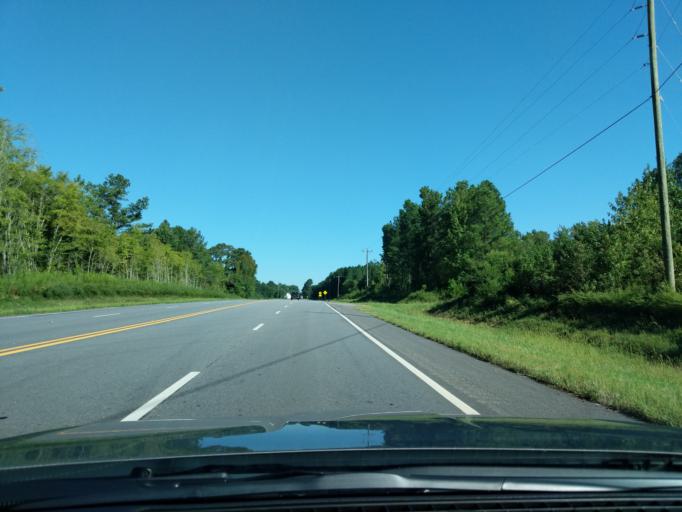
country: US
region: Georgia
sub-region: Oglethorpe County
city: Lexington
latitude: 33.8275
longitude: -83.0444
